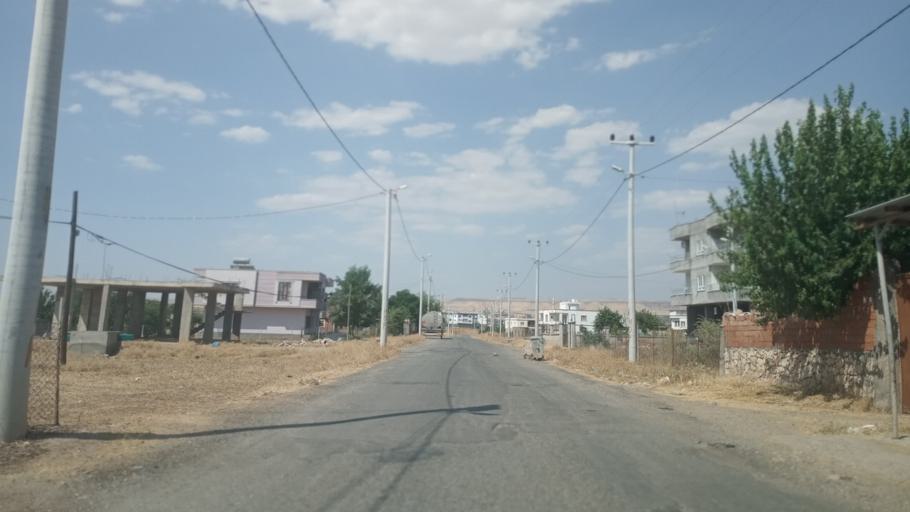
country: TR
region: Batman
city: Binatli
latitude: 37.8413
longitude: 41.2110
